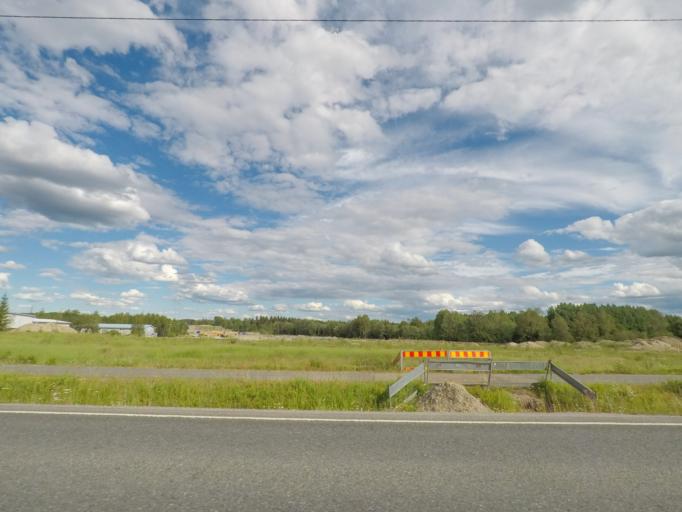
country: FI
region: Paijanne Tavastia
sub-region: Lahti
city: Lahti
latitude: 60.9553
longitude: 25.6173
